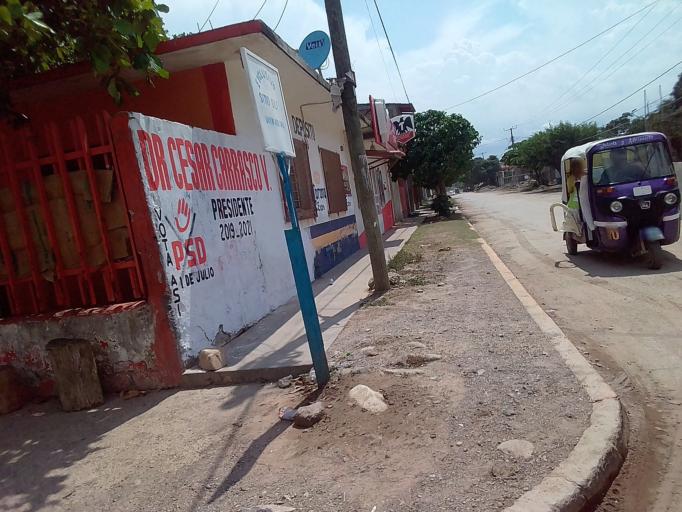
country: MX
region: Oaxaca
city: Union Hidalgo
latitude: 16.4681
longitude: -94.8285
